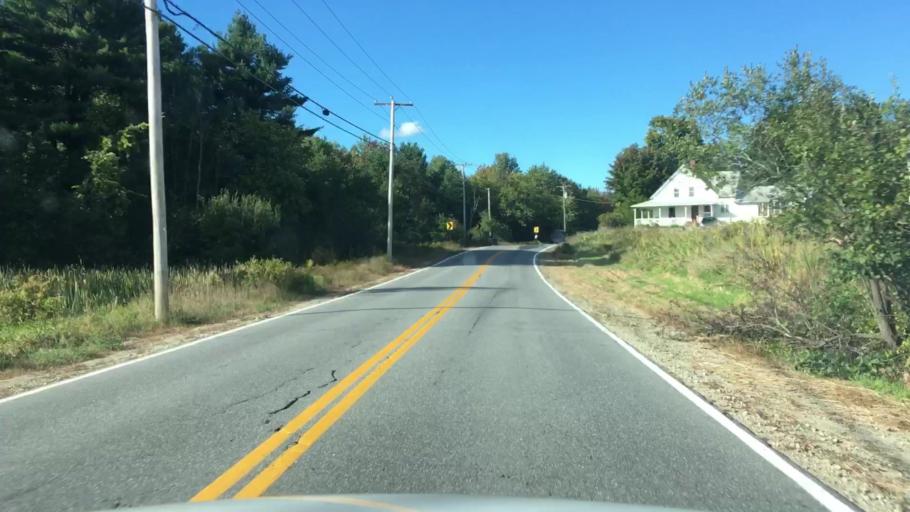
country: US
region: Maine
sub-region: Androscoggin County
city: Lisbon Falls
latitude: 43.9704
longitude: -70.0616
